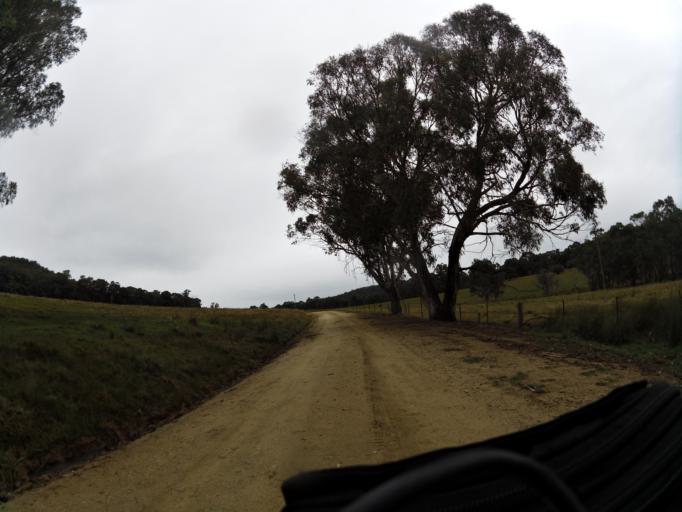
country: AU
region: New South Wales
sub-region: Greater Hume Shire
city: Holbrook
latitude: -36.1632
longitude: 147.4949
